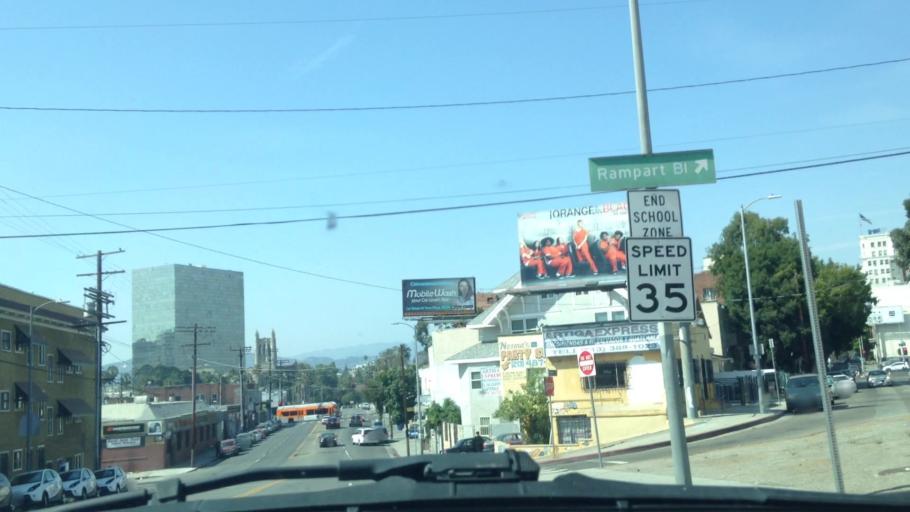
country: US
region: California
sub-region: Los Angeles County
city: Echo Park
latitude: 34.0580
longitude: -118.2842
